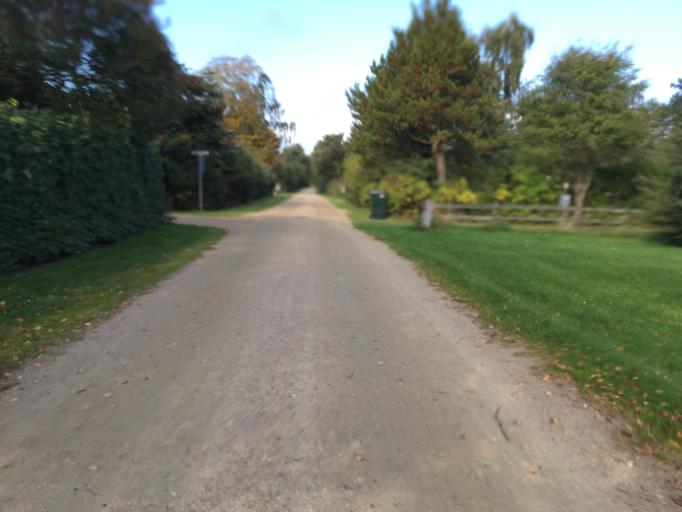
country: DK
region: Zealand
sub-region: Odsherred Kommune
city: Hojby
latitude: 55.8976
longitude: 11.5618
